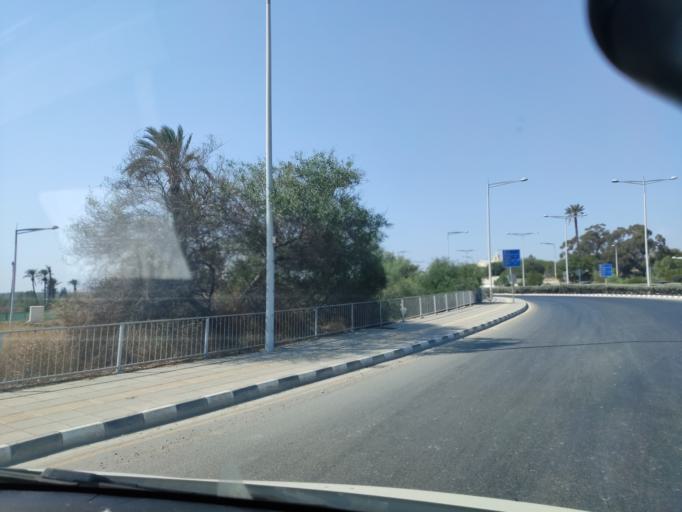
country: CY
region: Lefkosia
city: Geri
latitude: 35.1424
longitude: 33.4053
